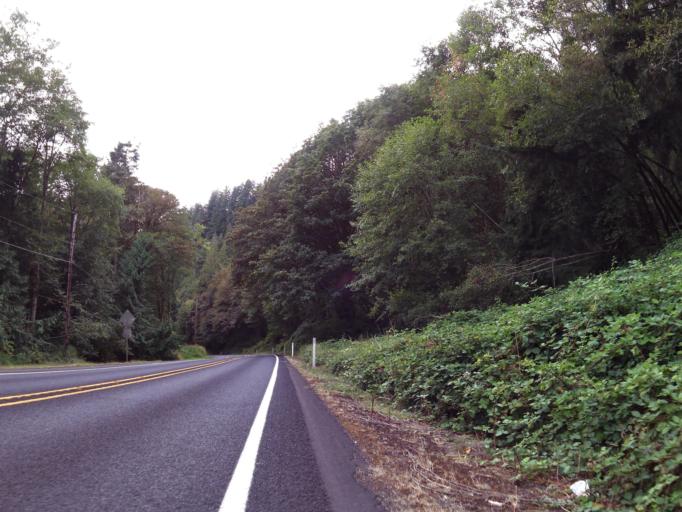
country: US
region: Oregon
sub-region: Columbia County
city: Clatskanie
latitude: 46.1731
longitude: -123.2305
